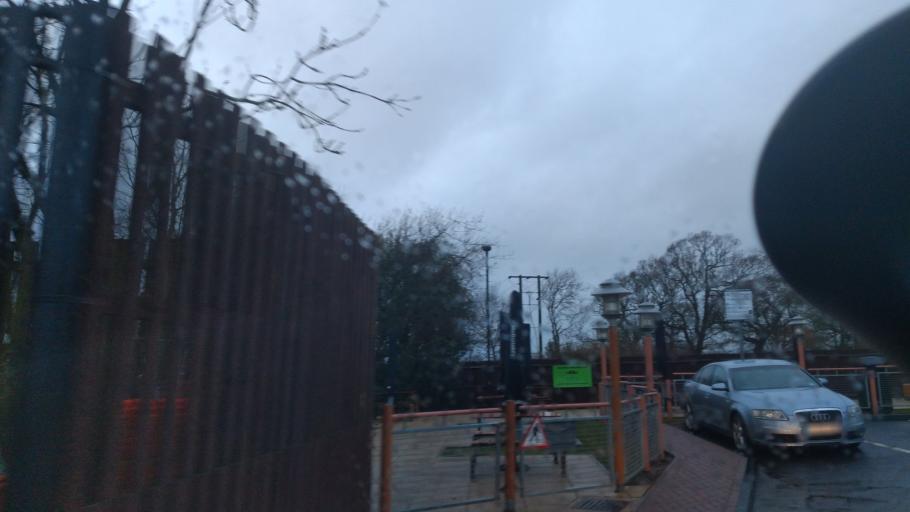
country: GB
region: England
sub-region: West Sussex
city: Arundel
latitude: 50.8433
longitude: -0.5428
